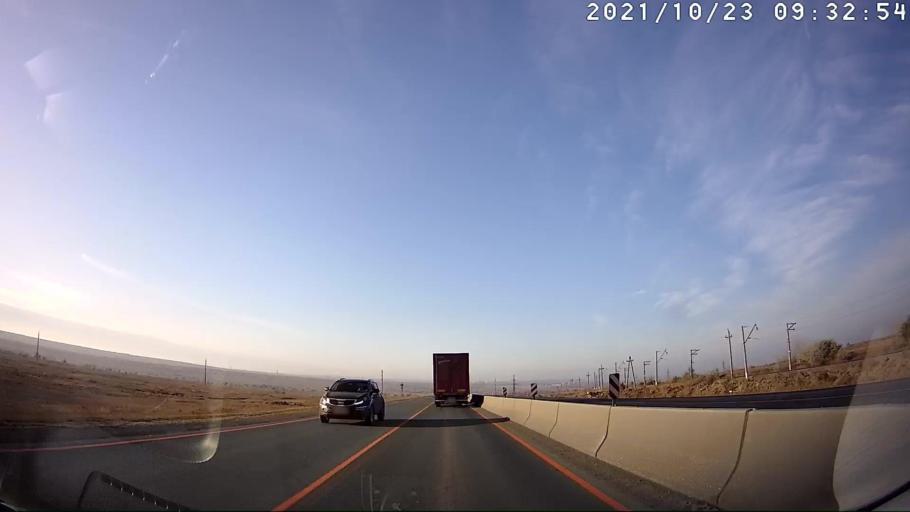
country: RU
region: Saratov
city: Sokolovyy
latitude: 51.6660
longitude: 45.8559
